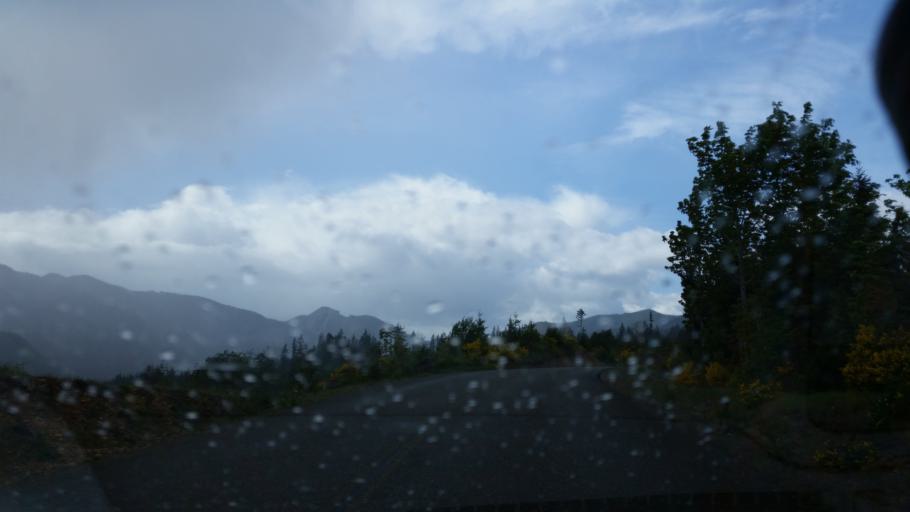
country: US
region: Washington
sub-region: Mason County
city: Shelton
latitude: 47.3247
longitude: -123.2772
